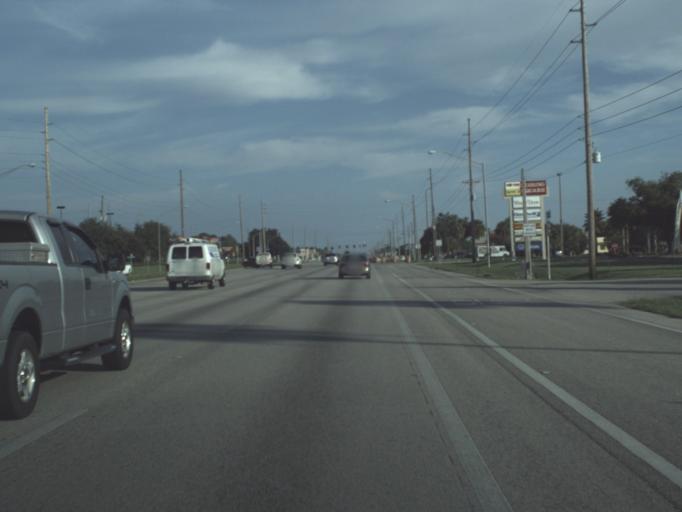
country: US
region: Florida
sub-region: Highlands County
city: Sebring
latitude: 27.5112
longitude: -81.4936
